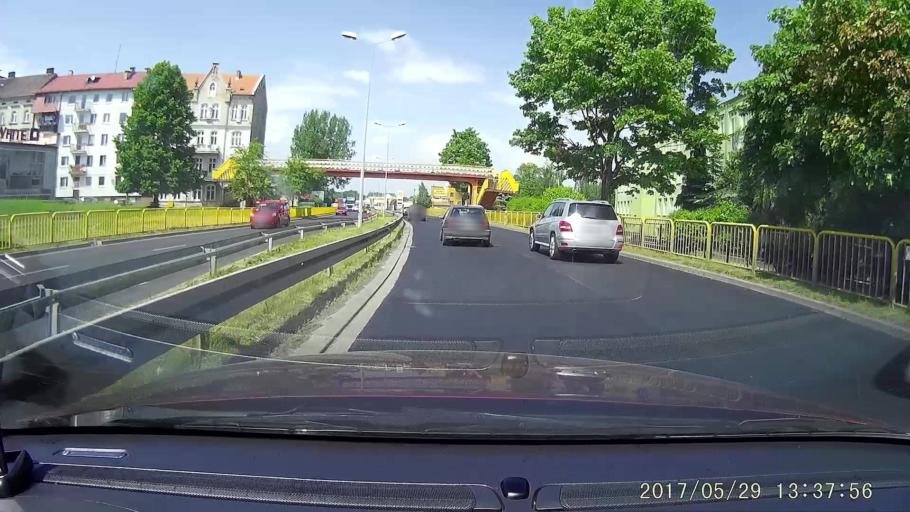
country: PL
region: Lower Silesian Voivodeship
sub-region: Powiat lubanski
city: Luban
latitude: 51.1187
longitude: 15.2952
